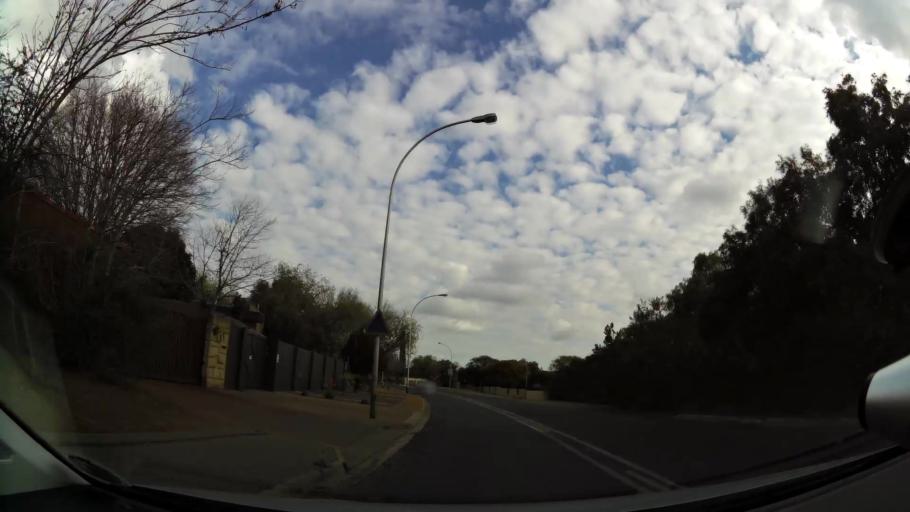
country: ZA
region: Orange Free State
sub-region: Mangaung Metropolitan Municipality
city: Bloemfontein
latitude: -29.0773
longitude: 26.2060
